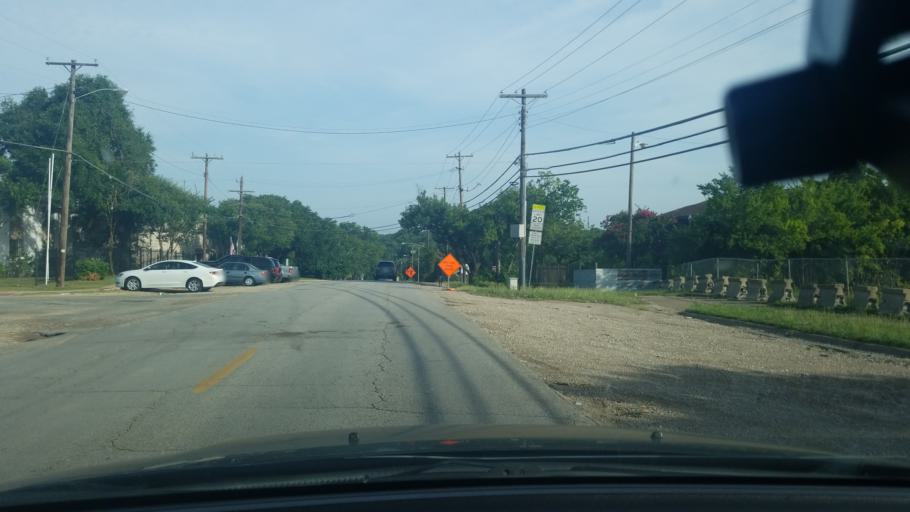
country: US
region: Texas
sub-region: Dallas County
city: Highland Park
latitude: 32.8025
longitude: -96.7148
